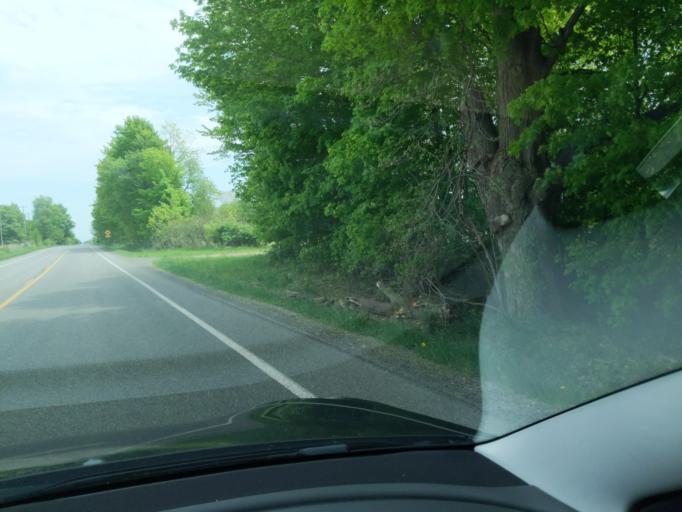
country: US
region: Michigan
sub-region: Ingham County
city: Mason
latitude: 42.5240
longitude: -84.5066
